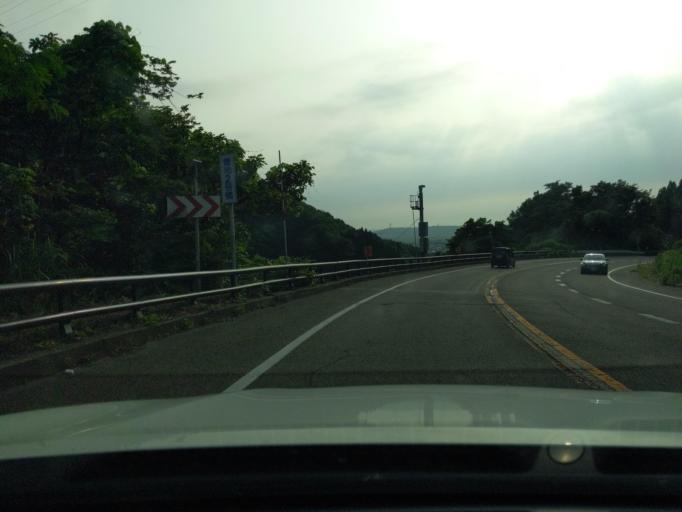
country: JP
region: Niigata
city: Kashiwazaki
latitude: 37.4051
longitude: 138.6561
